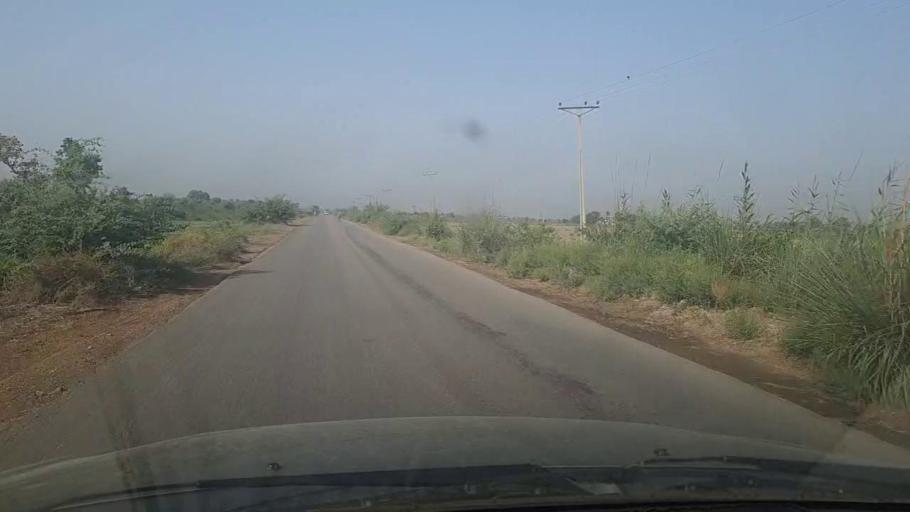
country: PK
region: Sindh
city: Tando Muhammad Khan
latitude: 25.0479
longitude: 68.4462
